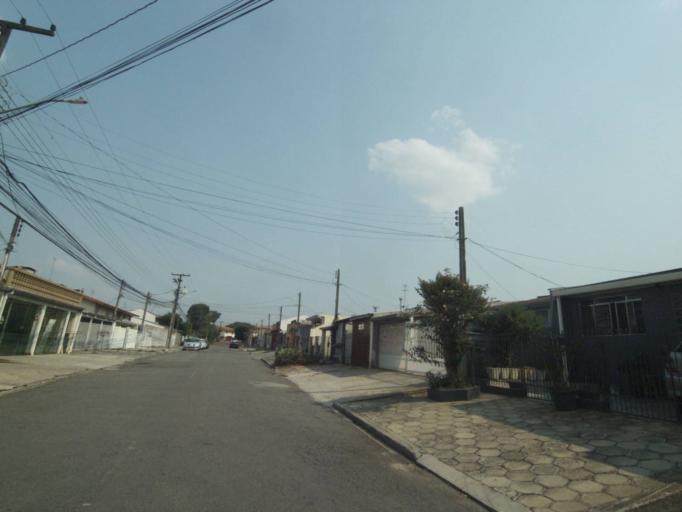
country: BR
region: Parana
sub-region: Sao Jose Dos Pinhais
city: Sao Jose dos Pinhais
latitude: -25.5286
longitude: -49.2430
